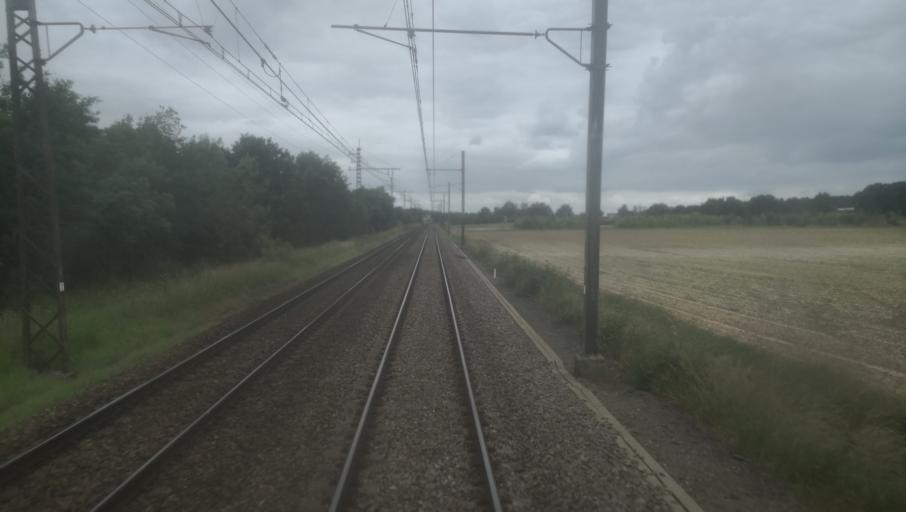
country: FR
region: Midi-Pyrenees
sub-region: Departement du Tarn-et-Garonne
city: Finhan
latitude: 43.9070
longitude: 1.2635
